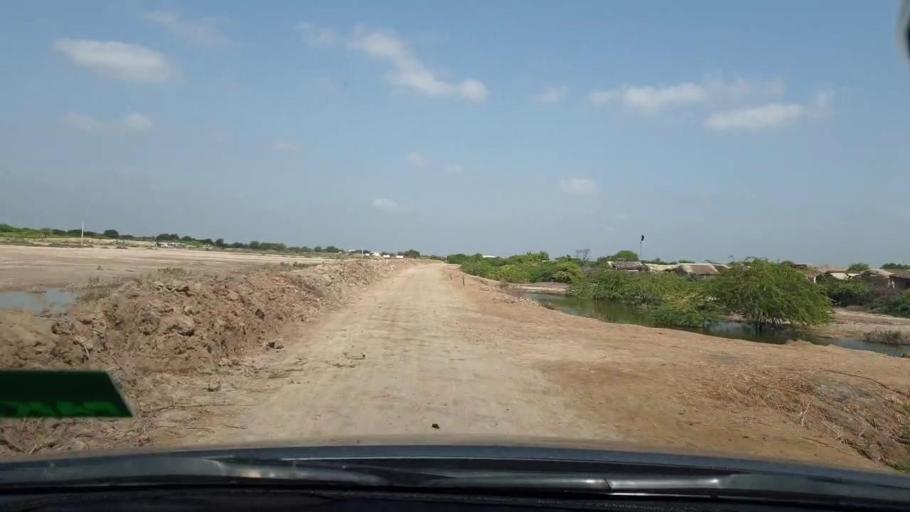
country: PK
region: Sindh
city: Tando Bago
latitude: 24.9477
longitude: 69.0753
